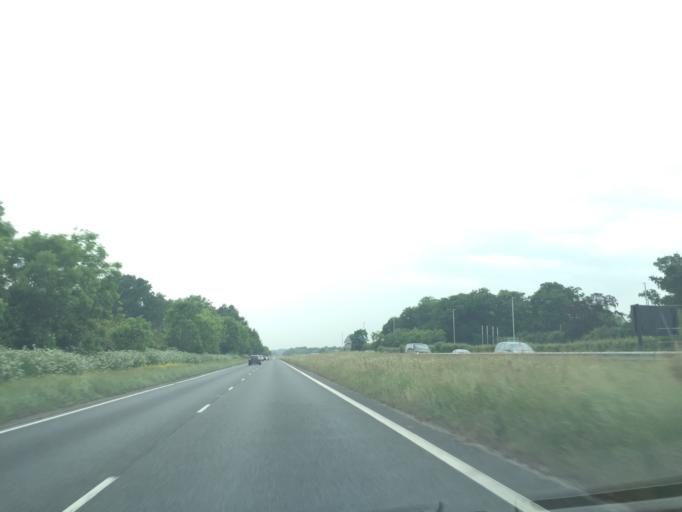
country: GB
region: England
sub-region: Poole
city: Poole
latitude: 50.7366
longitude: -2.0009
